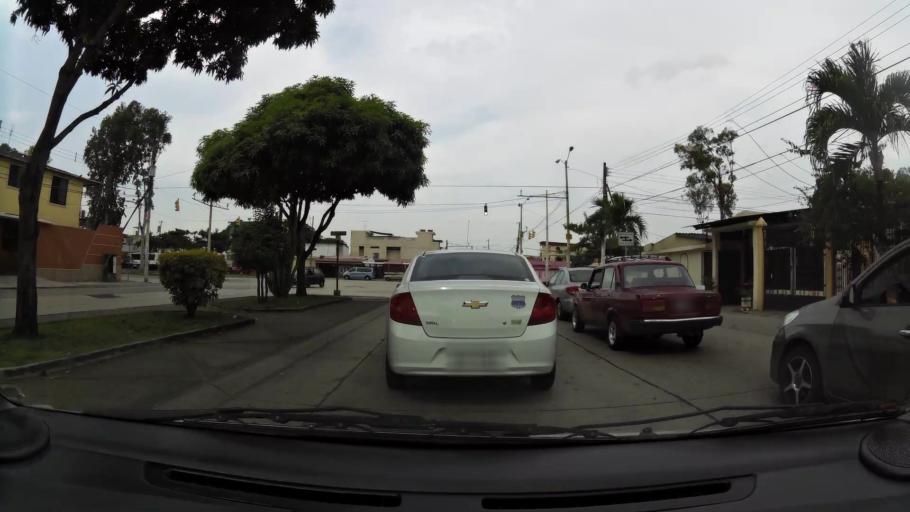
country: EC
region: Guayas
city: Eloy Alfaro
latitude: -2.1144
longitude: -79.8924
